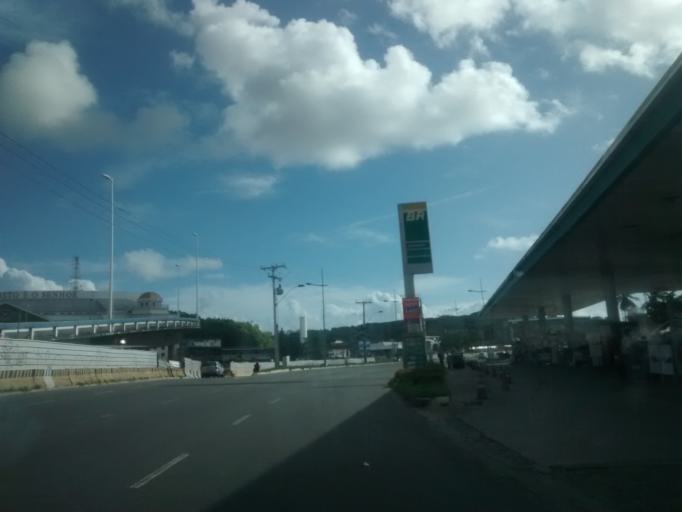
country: BR
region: Bahia
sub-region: Salvador
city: Salvador
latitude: -12.9791
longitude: -38.4650
